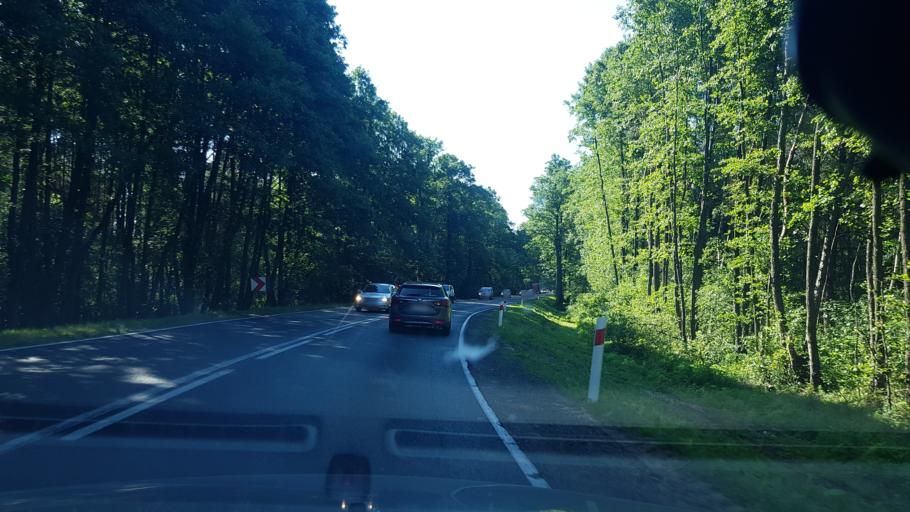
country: PL
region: Masovian Voivodeship
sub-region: Powiat wyszkowski
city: Branszczyk
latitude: 52.5801
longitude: 21.5334
